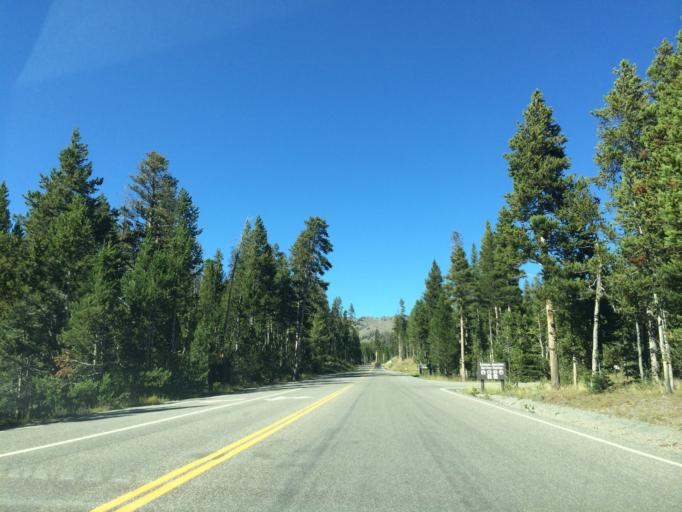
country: US
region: Montana
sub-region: Gallatin County
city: West Yellowstone
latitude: 44.7362
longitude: -110.4932
